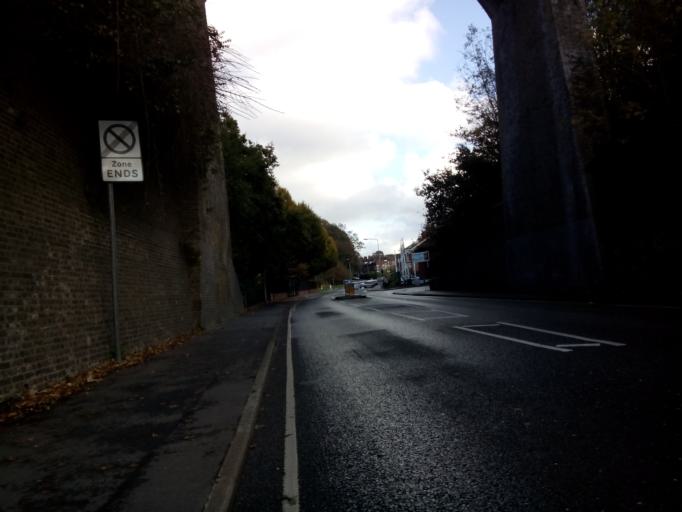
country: GB
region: England
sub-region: Suffolk
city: Ipswich
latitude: 52.0576
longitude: 1.1746
